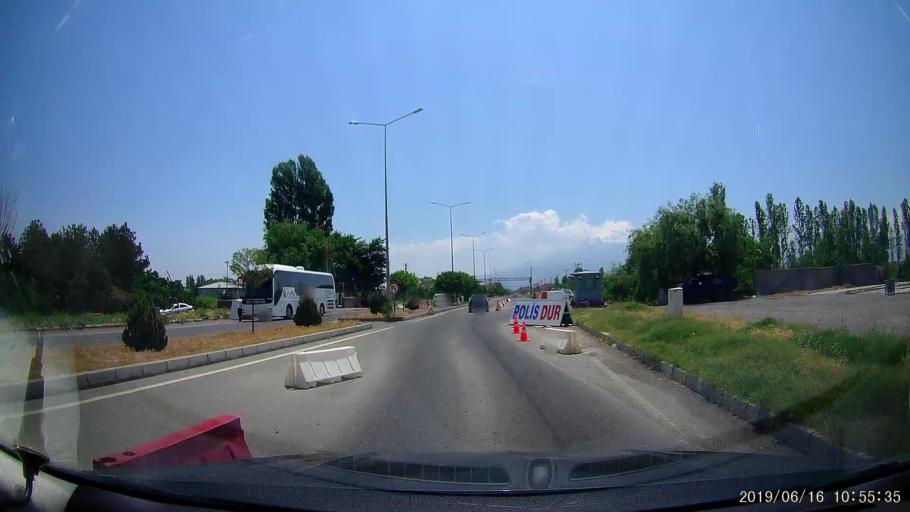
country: TR
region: Igdir
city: Igdir
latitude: 39.9355
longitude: 44.0119
